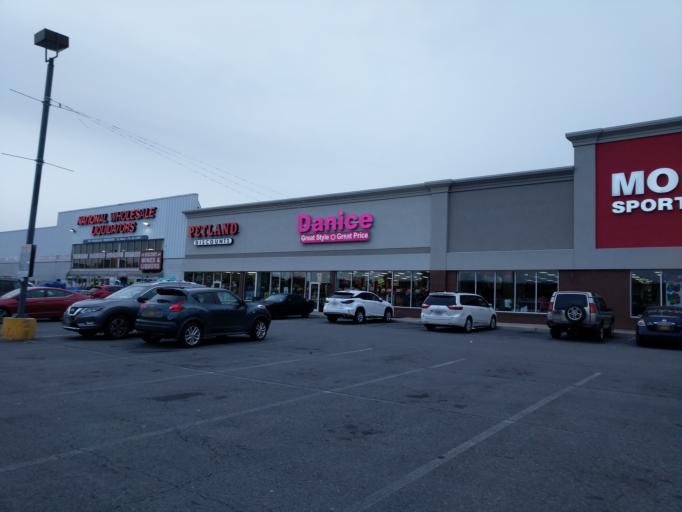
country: US
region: New York
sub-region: Queens County
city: Long Island City
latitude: 40.7527
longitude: -73.9164
